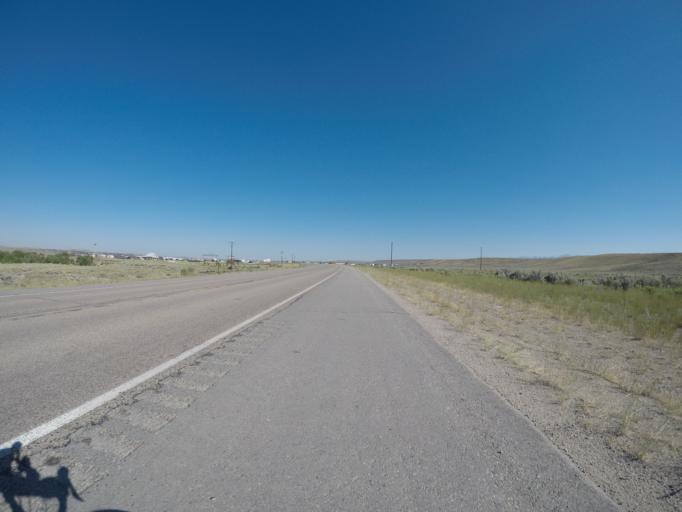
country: US
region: Wyoming
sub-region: Sublette County
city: Pinedale
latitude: 42.7582
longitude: -109.7321
